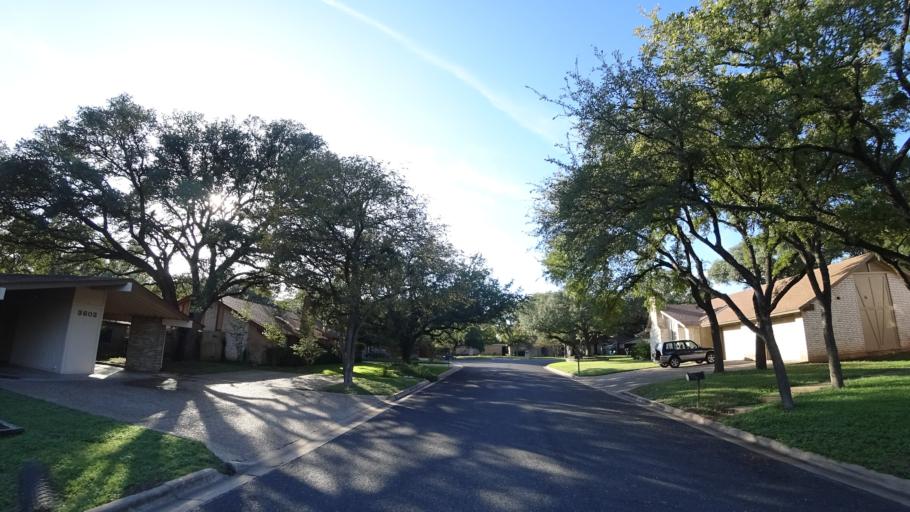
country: US
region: Texas
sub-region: Williamson County
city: Jollyville
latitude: 30.3667
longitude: -97.7468
